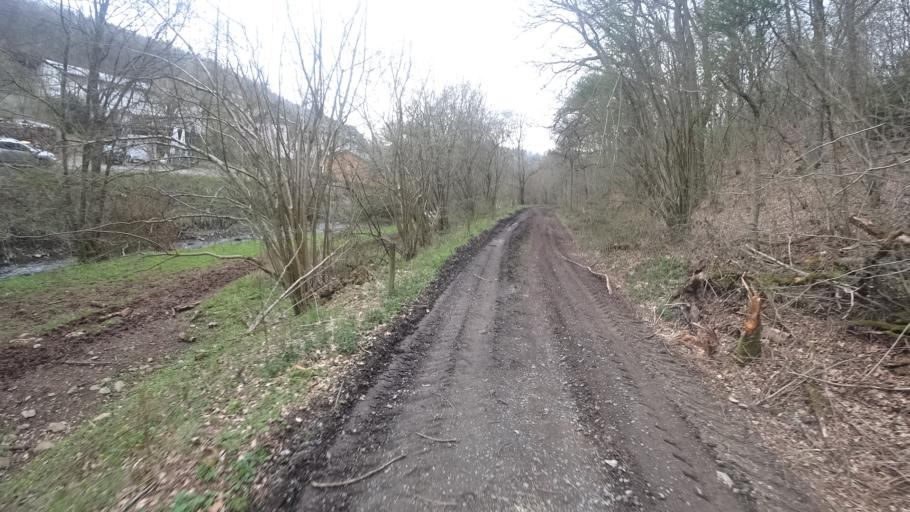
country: DE
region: Rheinland-Pfalz
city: Elben
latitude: 50.7632
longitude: 7.8353
